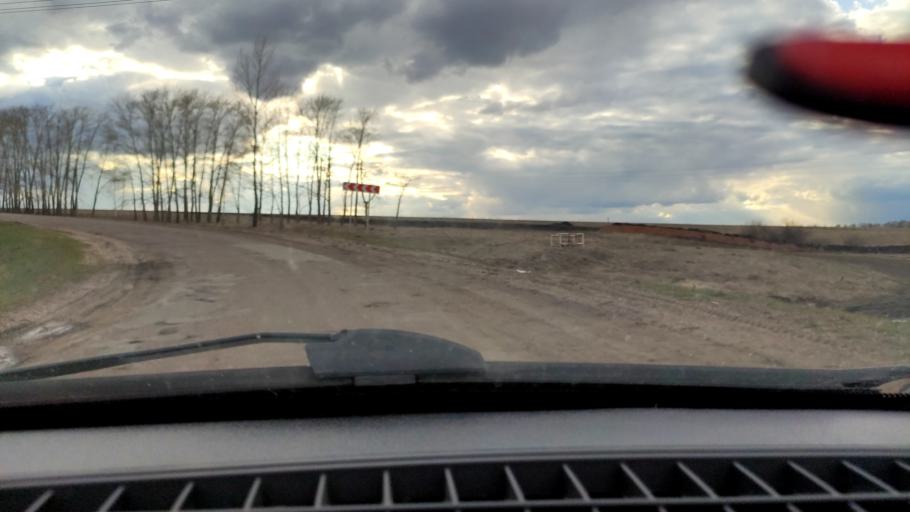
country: RU
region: Bashkortostan
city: Karmaskaly
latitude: 54.3104
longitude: 55.9443
